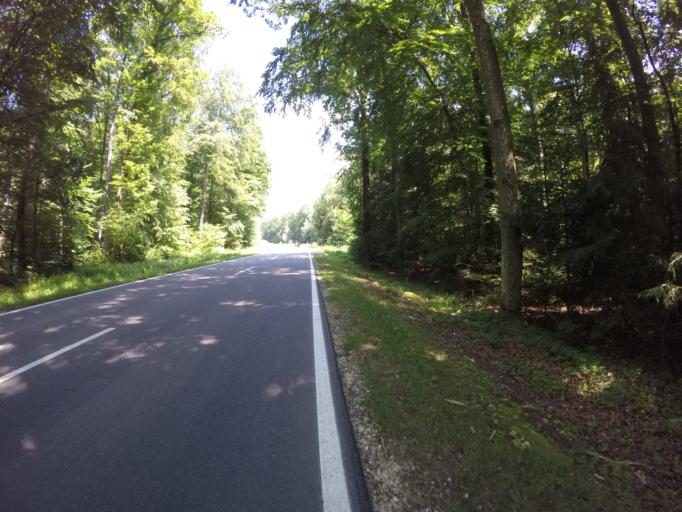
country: DE
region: Bavaria
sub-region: Lower Bavaria
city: Essing
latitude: 48.9085
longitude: 11.7851
